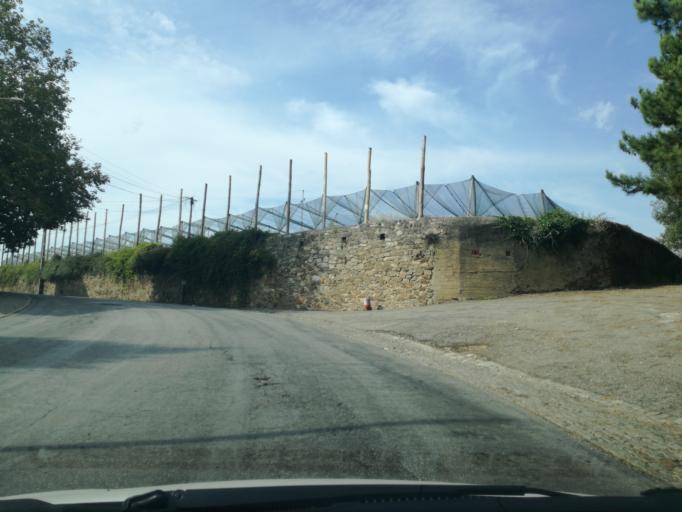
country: PT
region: Porto
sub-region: Vila Nova de Gaia
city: Azenha
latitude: 41.0608
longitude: -8.6274
